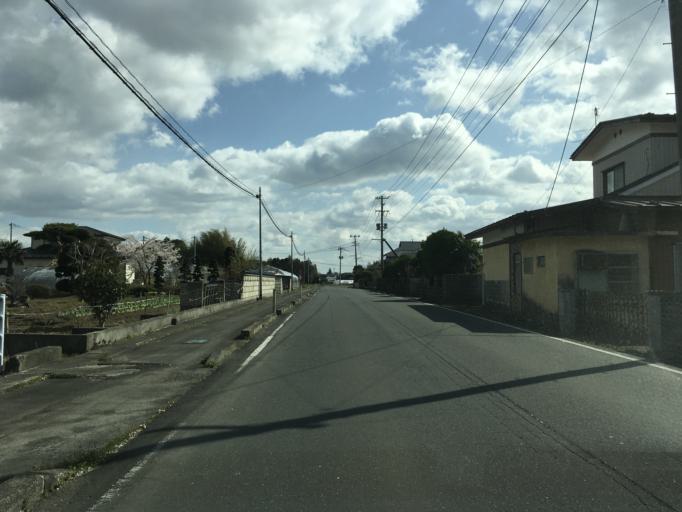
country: JP
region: Iwate
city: Ichinoseki
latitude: 38.7363
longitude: 141.2646
